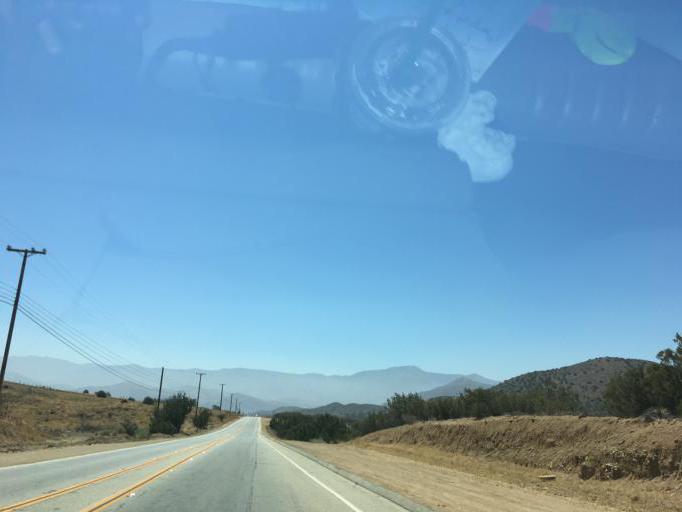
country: US
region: California
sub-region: Los Angeles County
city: Acton
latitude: 34.5079
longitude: -118.2329
